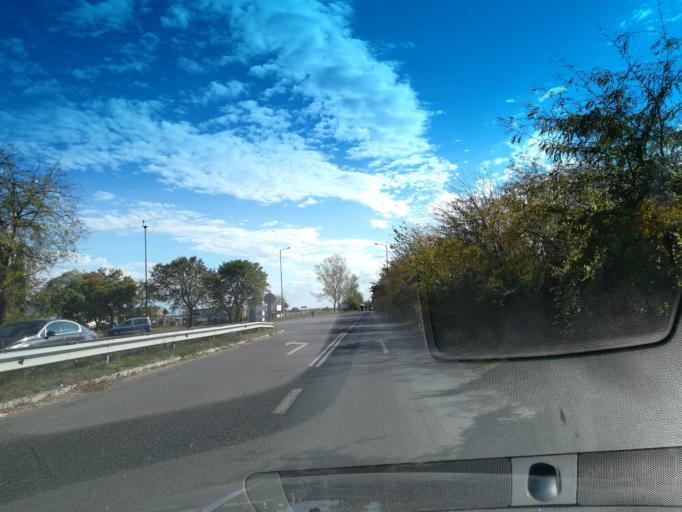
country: BG
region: Stara Zagora
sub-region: Obshtina Stara Zagora
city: Stara Zagora
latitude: 42.3860
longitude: 25.6486
